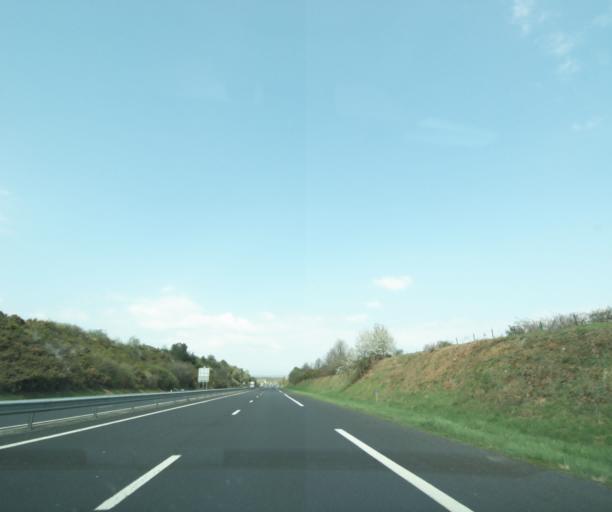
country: FR
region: Auvergne
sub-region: Departement de la Haute-Loire
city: Lempdes-sur-Allagnon
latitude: 45.3428
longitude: 3.2764
